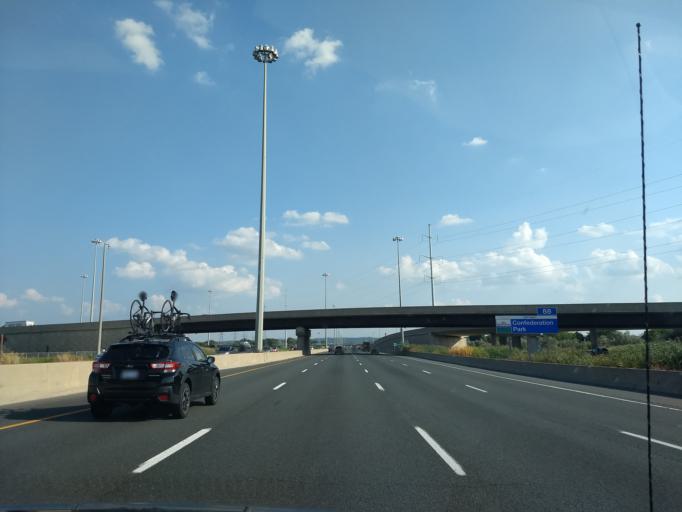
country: CA
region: Ontario
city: Hamilton
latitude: 43.2604
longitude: -79.7678
